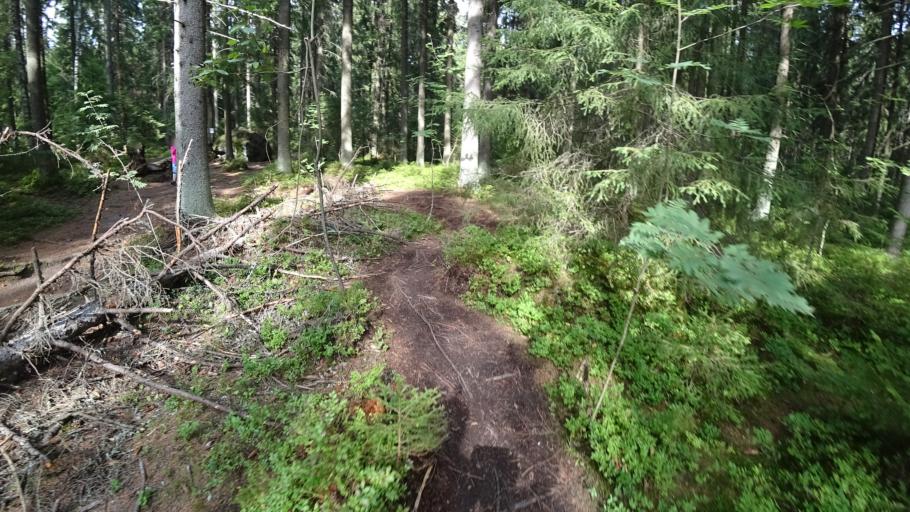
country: FI
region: Uusimaa
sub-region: Helsinki
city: Helsinki
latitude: 60.2601
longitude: 24.9203
